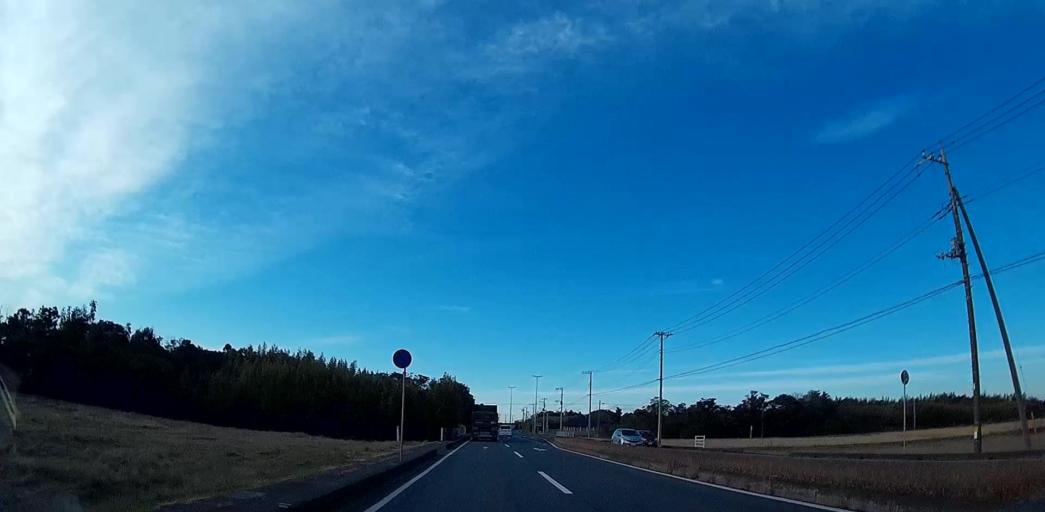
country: JP
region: Chiba
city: Omigawa
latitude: 35.8240
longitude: 140.7276
